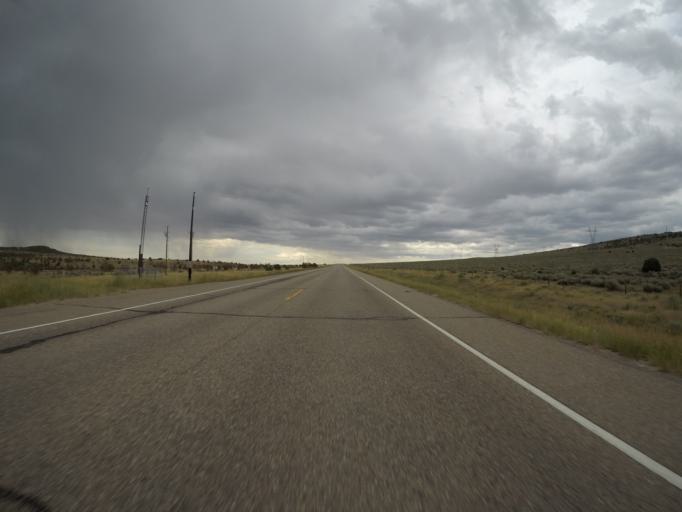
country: US
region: Colorado
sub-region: Rio Blanco County
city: Rangely
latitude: 40.3701
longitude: -108.3892
